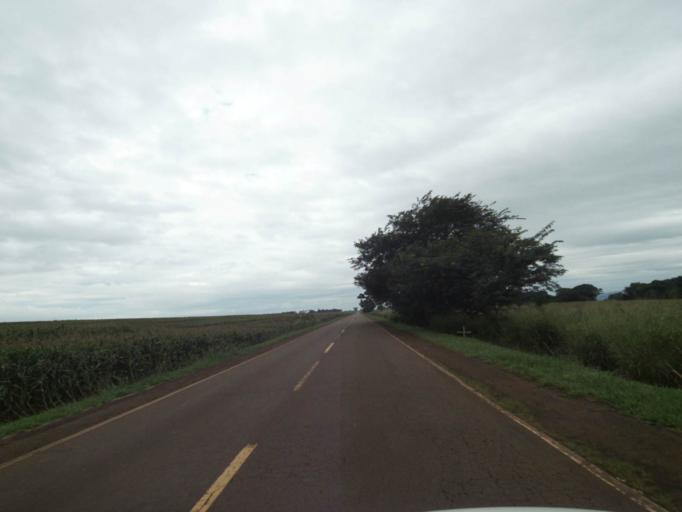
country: BR
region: Parana
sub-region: Marechal Candido Rondon
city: Marechal Candido Rondon
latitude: -24.8086
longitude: -54.1975
